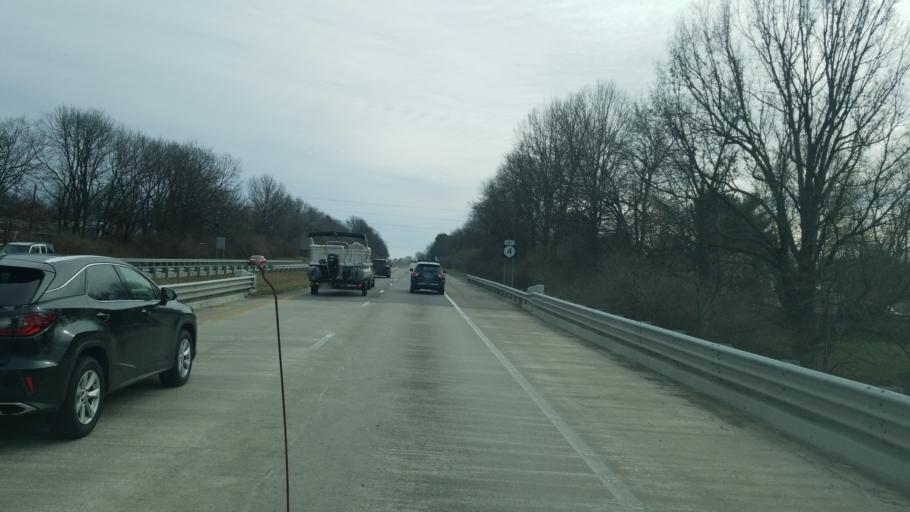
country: US
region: Kentucky
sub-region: Fayette County
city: Monticello
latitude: 37.9938
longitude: -84.5138
